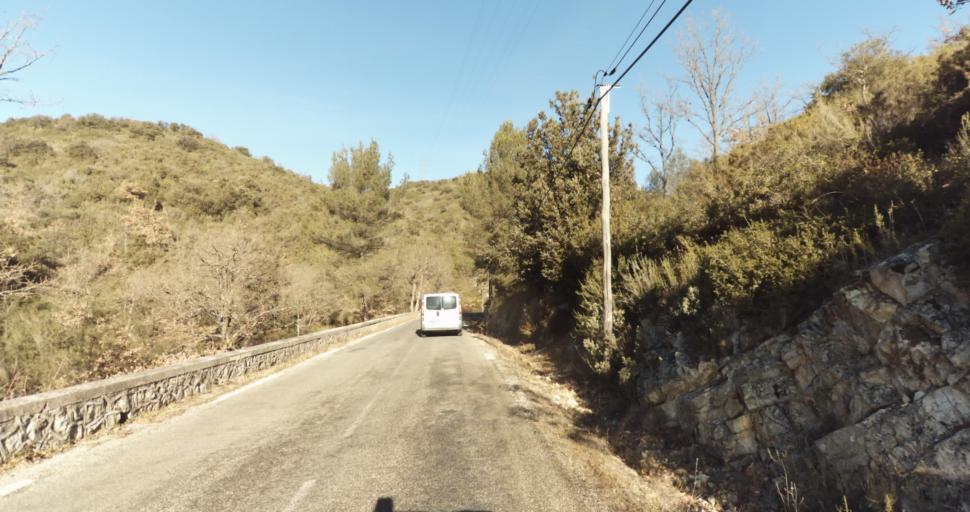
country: FR
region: Provence-Alpes-Cote d'Azur
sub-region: Departement des Bouches-du-Rhone
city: Peypin
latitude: 43.3722
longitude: 5.5640
